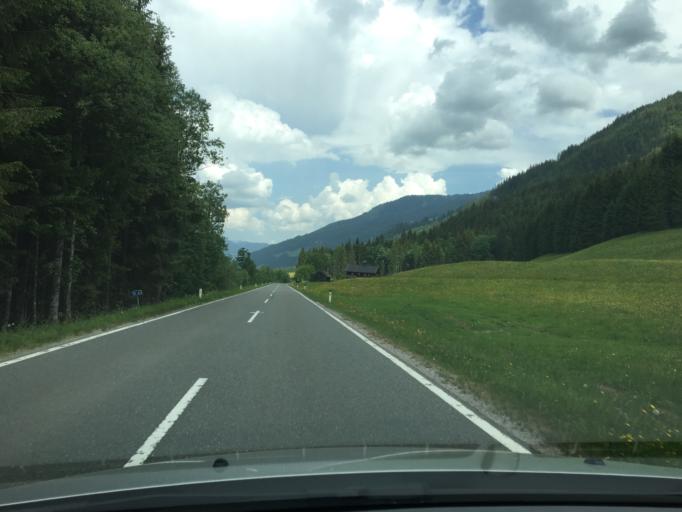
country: AT
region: Salzburg
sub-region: Politischer Bezirk Sankt Johann im Pongau
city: Kleinarl
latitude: 47.2484
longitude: 13.3281
